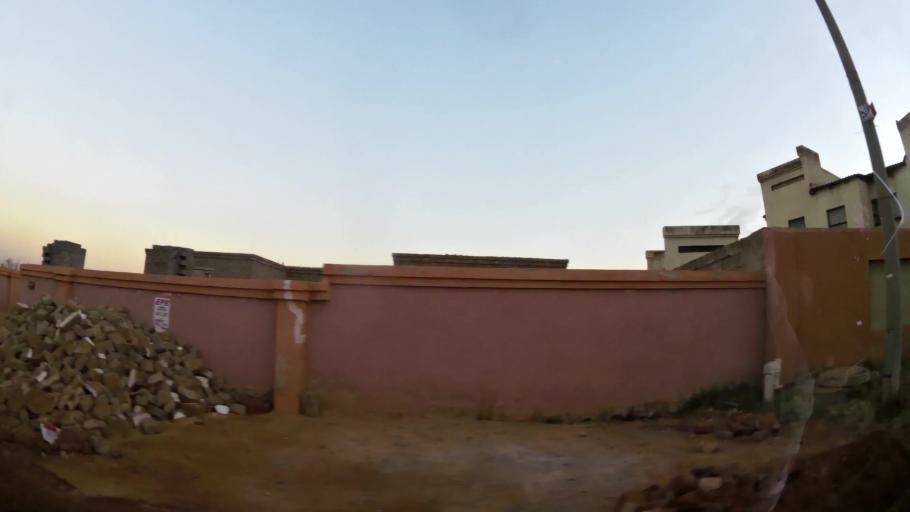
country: ZA
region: Gauteng
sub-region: West Rand District Municipality
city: Randfontein
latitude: -26.2117
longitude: 27.7083
